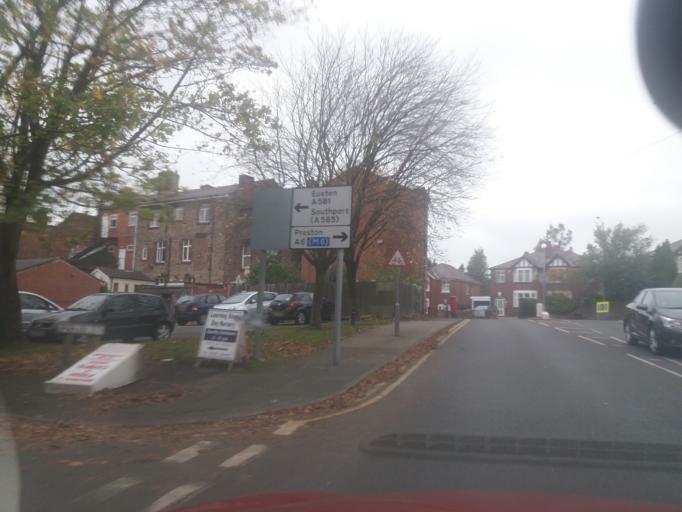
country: GB
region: England
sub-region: Lancashire
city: Chorley
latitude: 53.6591
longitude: -2.6301
